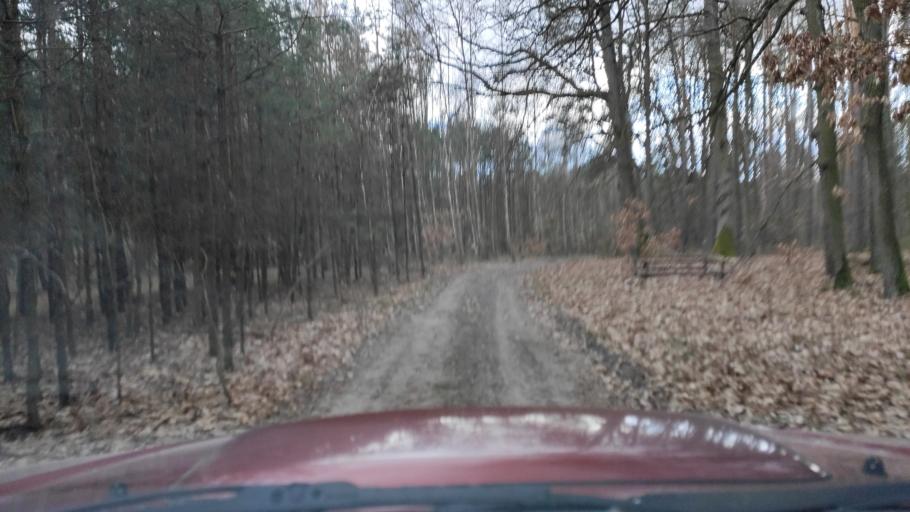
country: PL
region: Masovian Voivodeship
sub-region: Powiat kozienicki
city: Garbatka-Letnisko
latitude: 51.5090
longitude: 21.5616
